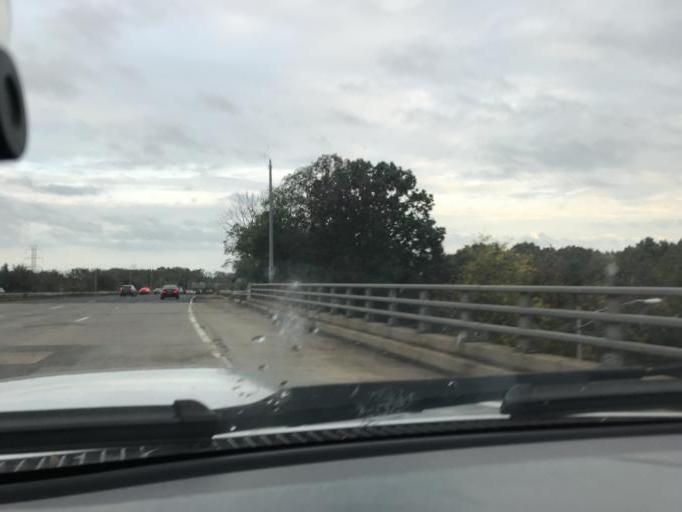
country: US
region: New Jersey
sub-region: Mercer County
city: Lawrenceville
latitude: 40.2835
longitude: -74.6966
